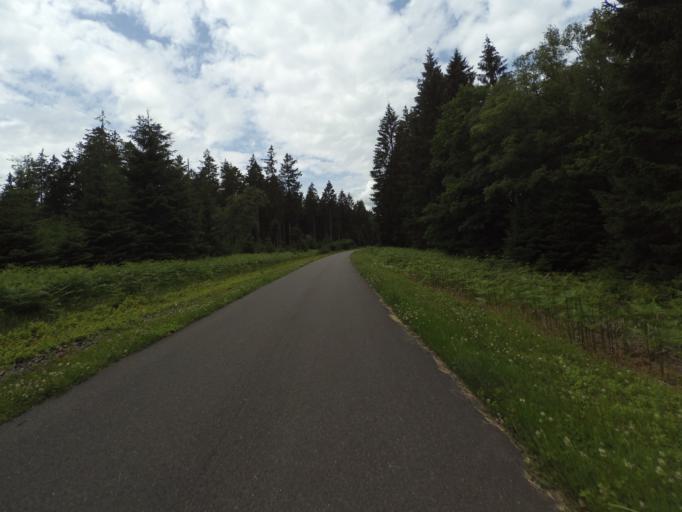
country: DE
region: North Rhine-Westphalia
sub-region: Regierungsbezirk Koln
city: Roetgen
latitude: 50.6414
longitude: 6.2433
